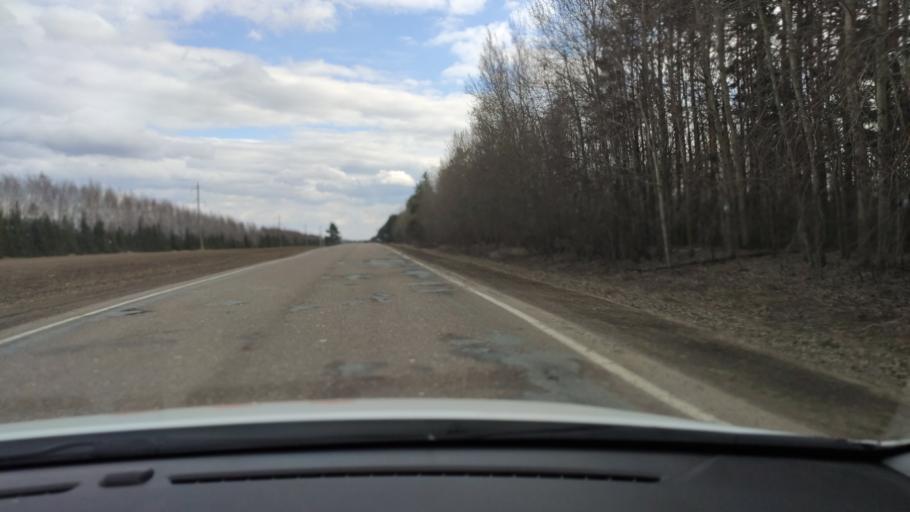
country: RU
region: Tatarstan
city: Vysokaya Gora
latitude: 56.0608
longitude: 49.2051
